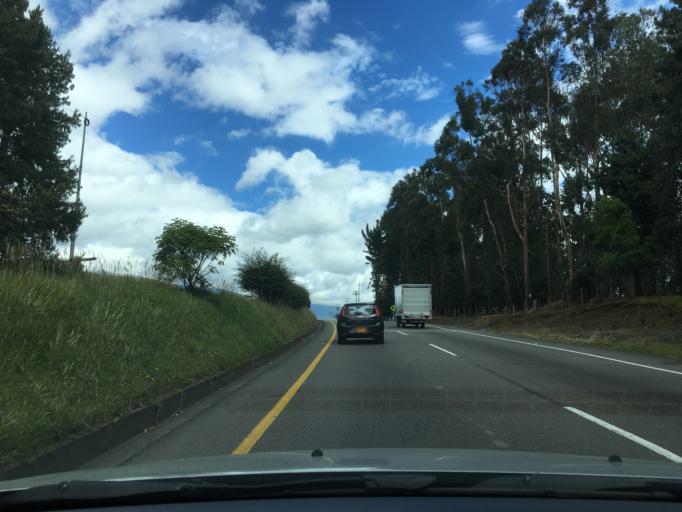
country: CO
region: Boyaca
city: Tuta
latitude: 5.6711
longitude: -73.2694
